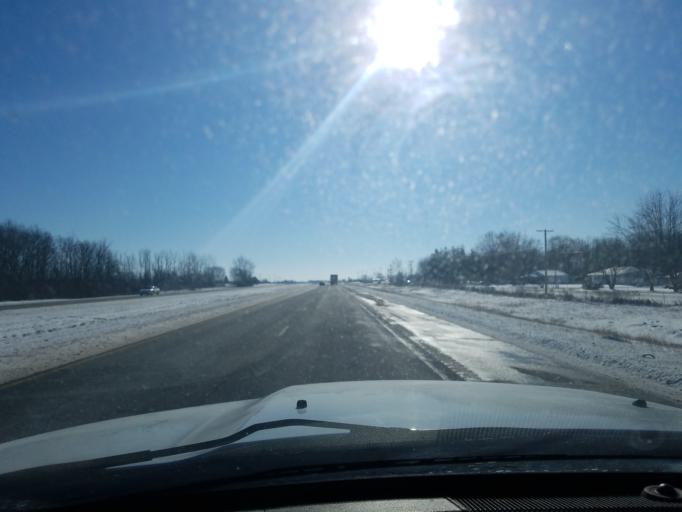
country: US
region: Indiana
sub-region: Noble County
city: Kendallville
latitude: 41.4071
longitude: -85.2562
